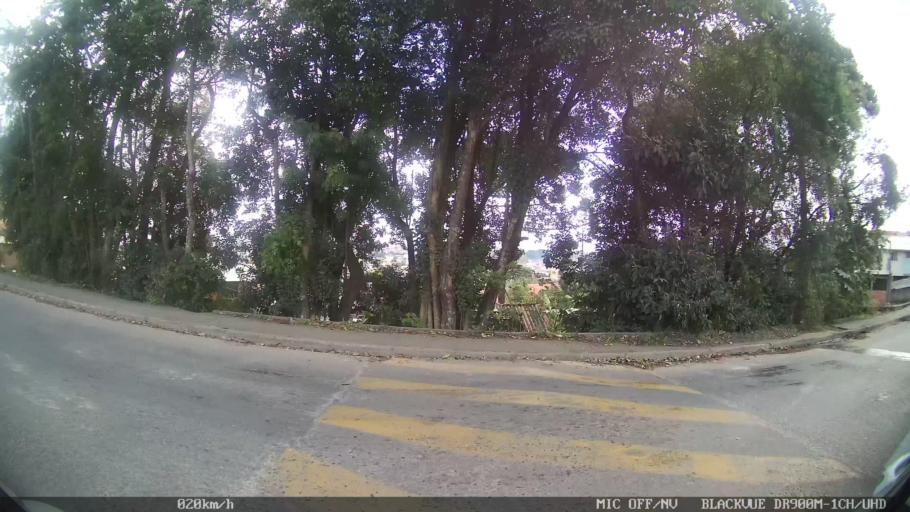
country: BR
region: Parana
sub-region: Colombo
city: Colombo
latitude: -25.3618
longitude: -49.1910
